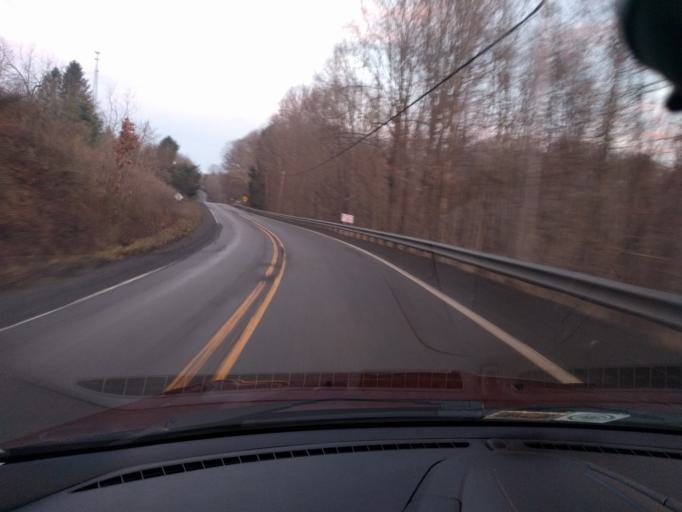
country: US
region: West Virginia
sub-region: Greenbrier County
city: Rainelle
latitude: 38.0075
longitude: -80.8786
